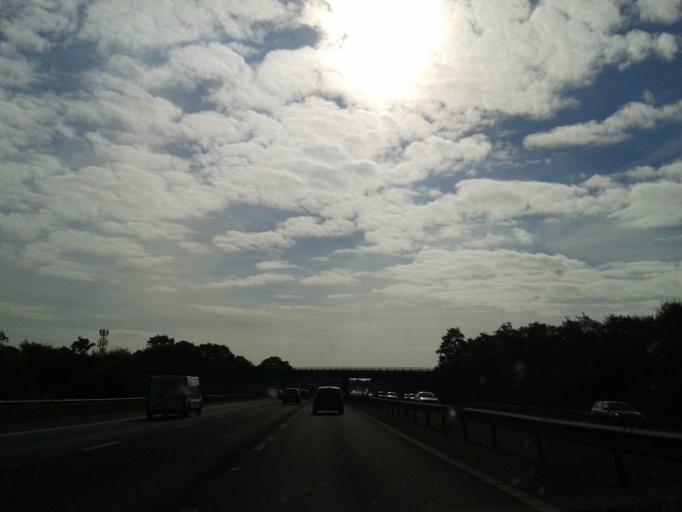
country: GB
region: England
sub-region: Cheshire East
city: Holmes Chapel
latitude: 53.1886
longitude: -2.3770
